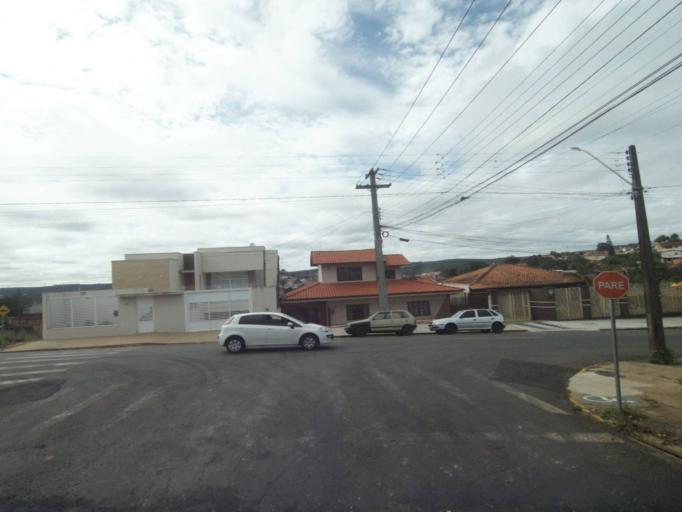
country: BR
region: Parana
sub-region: Telemaco Borba
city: Telemaco Borba
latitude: -24.3336
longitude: -50.6199
